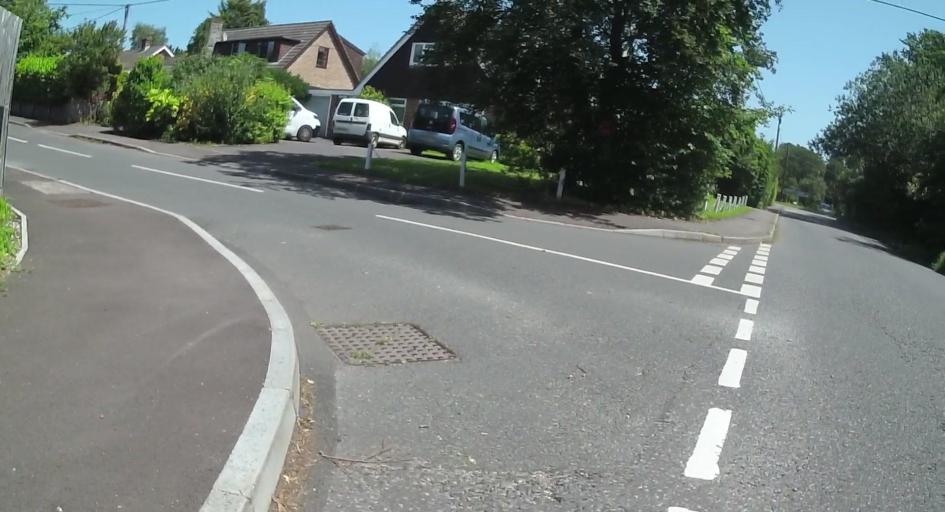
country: GB
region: England
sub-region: Hampshire
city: Kingsley
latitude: 51.1685
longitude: -0.8484
